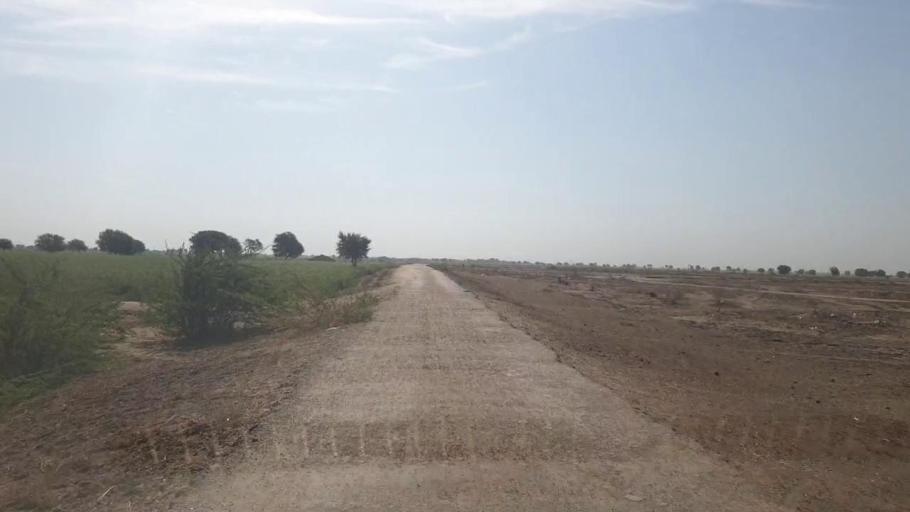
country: PK
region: Sindh
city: Umarkot
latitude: 25.2880
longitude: 69.6533
